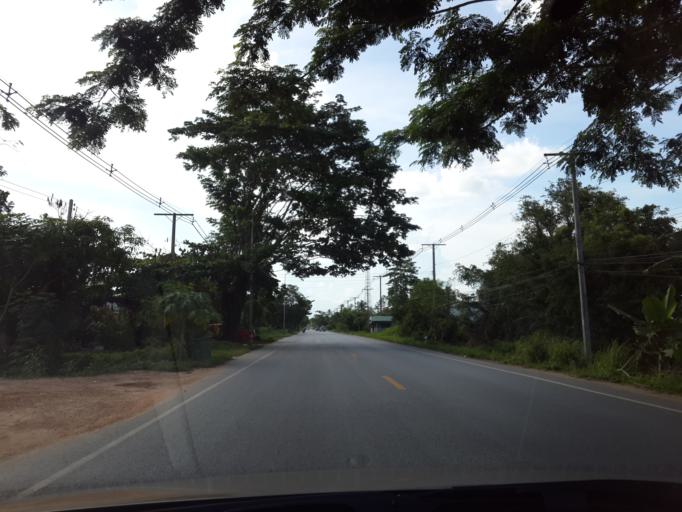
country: TH
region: Yala
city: Yala
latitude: 6.4832
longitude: 101.3156
